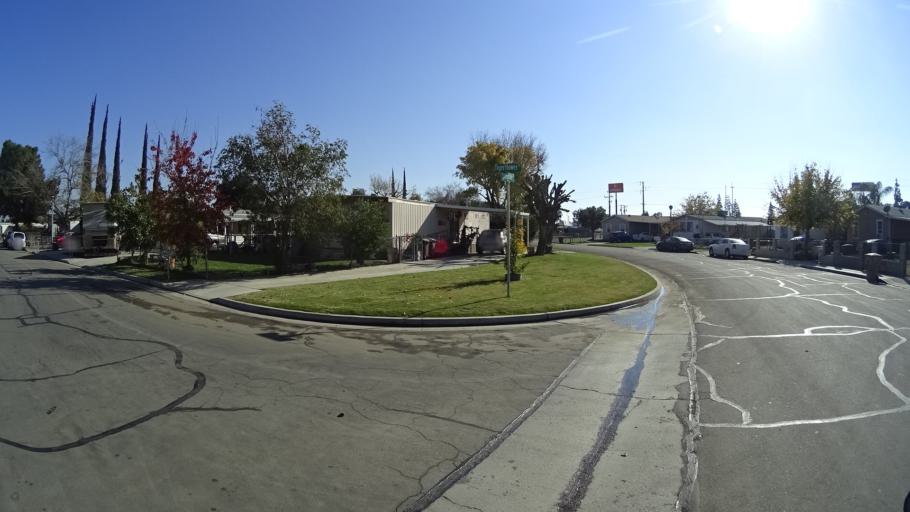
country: US
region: California
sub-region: Kern County
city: Greenfield
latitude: 35.2975
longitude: -119.0339
